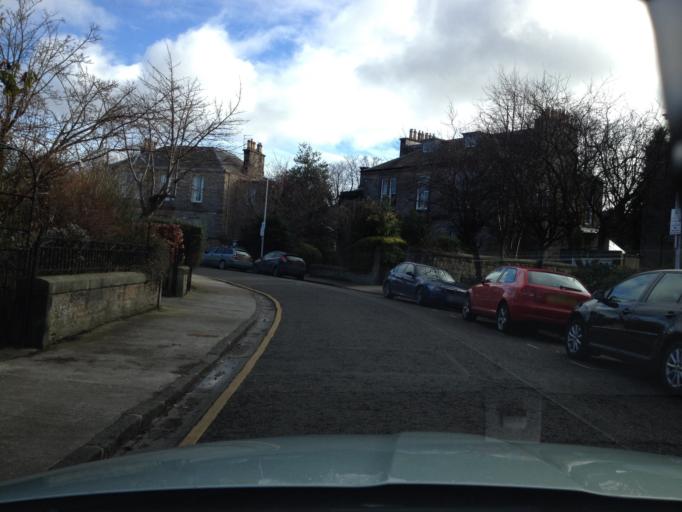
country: GB
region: Scotland
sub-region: Edinburgh
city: Edinburgh
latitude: 55.9320
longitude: -3.2128
